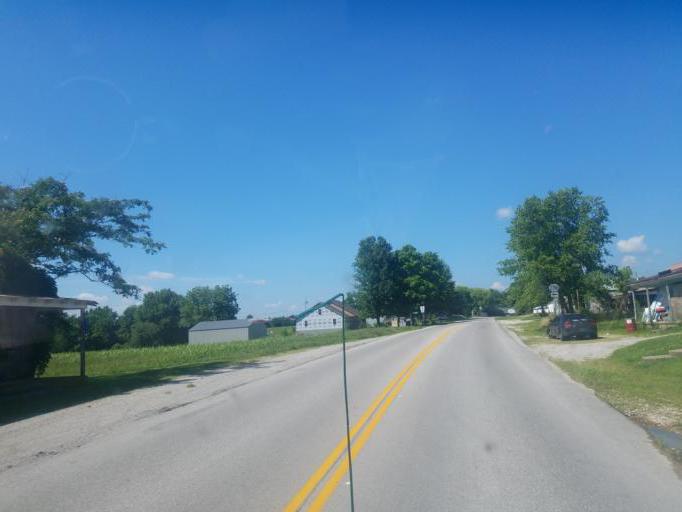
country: US
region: Kentucky
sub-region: Hart County
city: Munfordville
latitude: 37.3060
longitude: -85.9594
